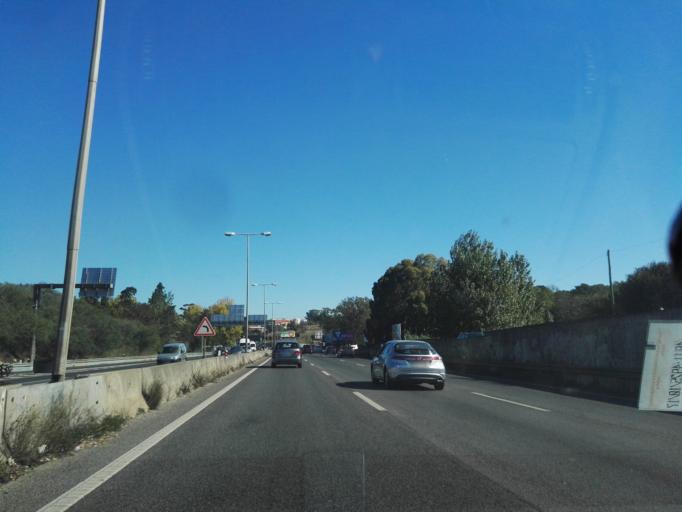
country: PT
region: Lisbon
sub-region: Sintra
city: Queluz
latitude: 38.7476
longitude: -9.2618
